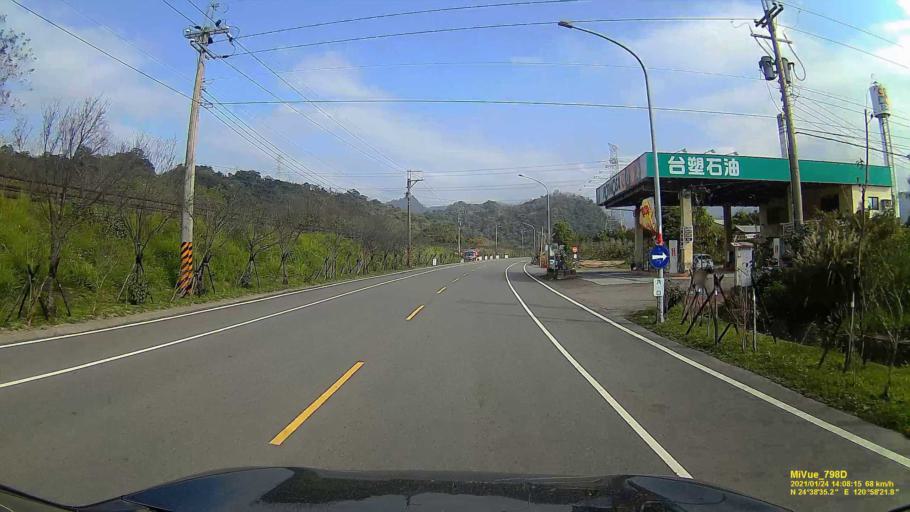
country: TW
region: Taiwan
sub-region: Hsinchu
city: Hsinchu
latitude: 24.6431
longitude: 120.9733
